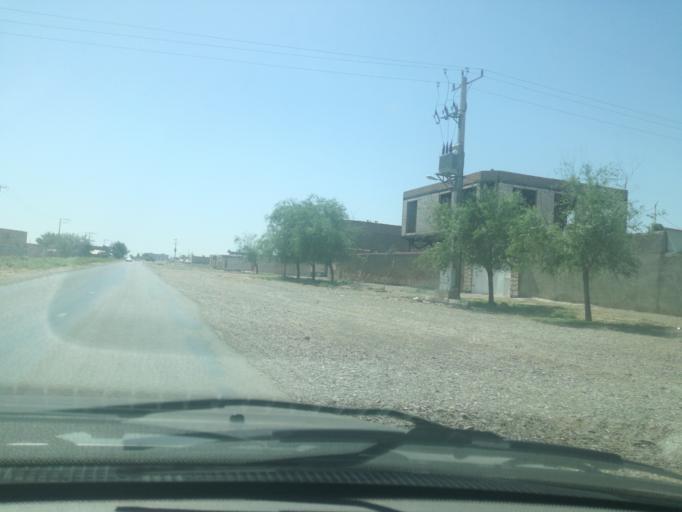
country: IR
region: Razavi Khorasan
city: Sarakhs
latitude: 36.5654
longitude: 61.1429
